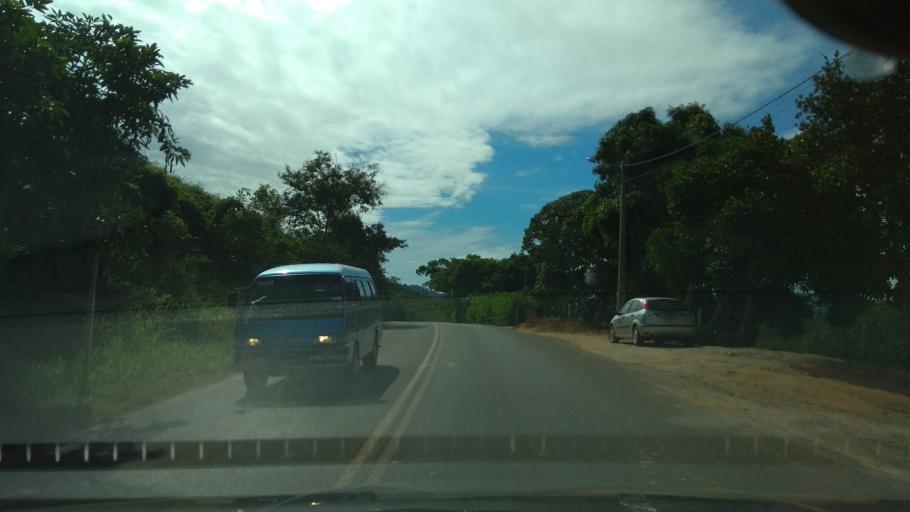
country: BR
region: Bahia
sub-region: Ubaira
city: Ubaira
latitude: -13.2708
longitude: -39.6539
